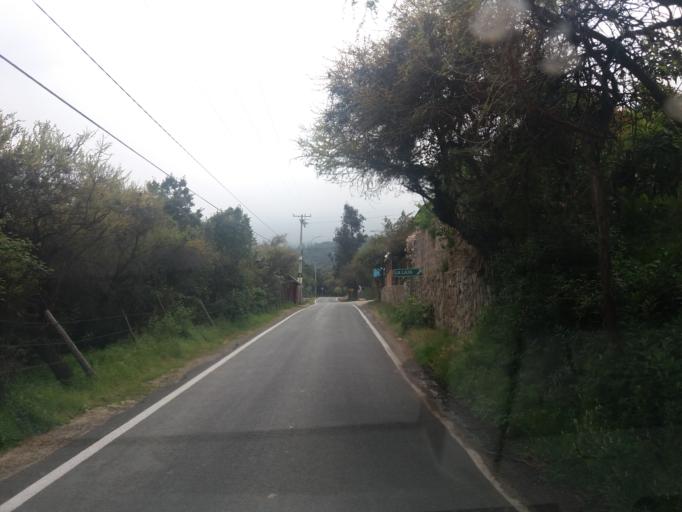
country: CL
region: Valparaiso
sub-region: Provincia de Marga Marga
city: Limache
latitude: -33.0265
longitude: -71.0768
